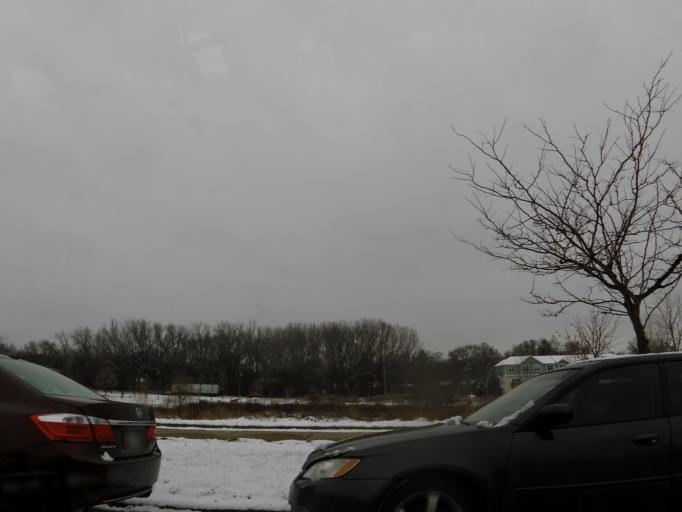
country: US
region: Minnesota
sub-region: Ramsey County
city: Maplewood
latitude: 44.9754
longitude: -93.0420
